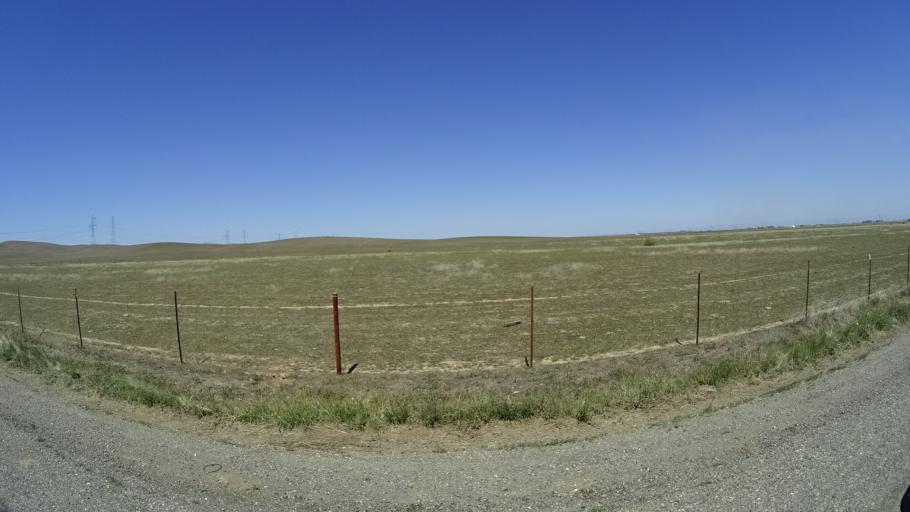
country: US
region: California
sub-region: Glenn County
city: Willows
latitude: 39.3997
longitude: -122.2800
